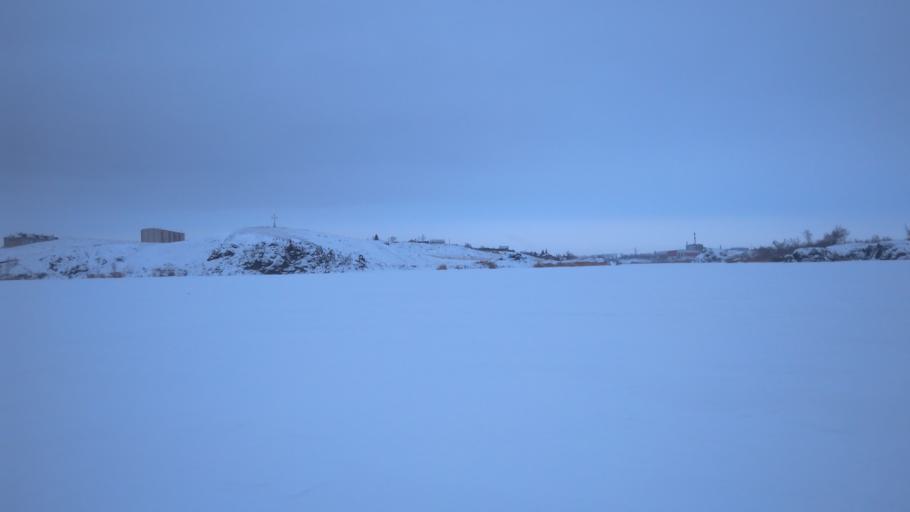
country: RU
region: Chelyabinsk
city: Troitsk
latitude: 54.0800
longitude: 61.5740
